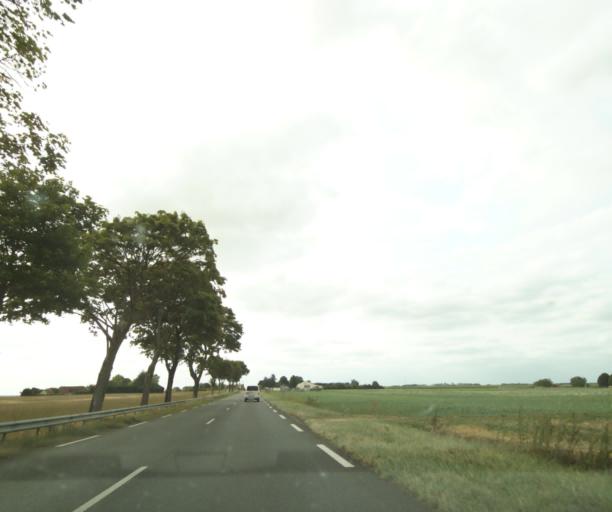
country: FR
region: Centre
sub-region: Departement d'Indre-et-Loire
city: Reignac-sur-Indre
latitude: 47.1944
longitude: 0.9237
